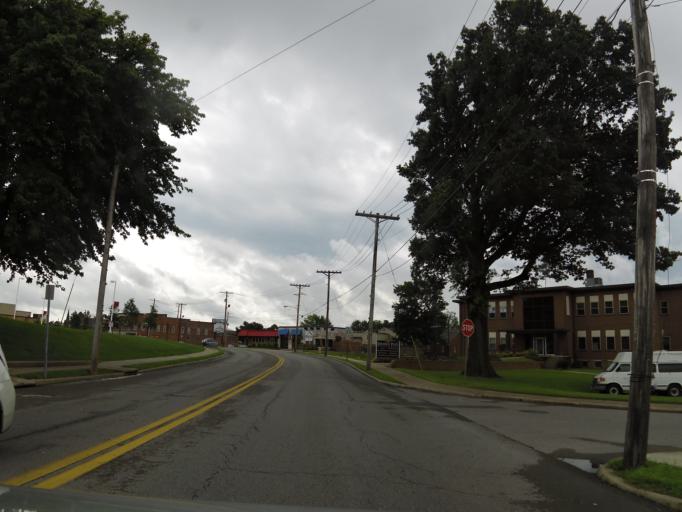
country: US
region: Missouri
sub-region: Cape Girardeau County
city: Cape Girardeau
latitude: 37.3076
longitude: -89.5313
